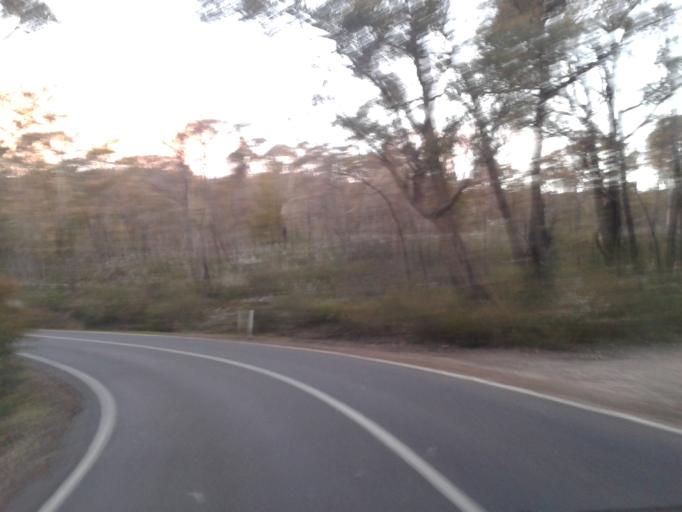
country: AU
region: Victoria
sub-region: Northern Grampians
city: Stawell
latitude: -37.1539
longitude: 142.4820
